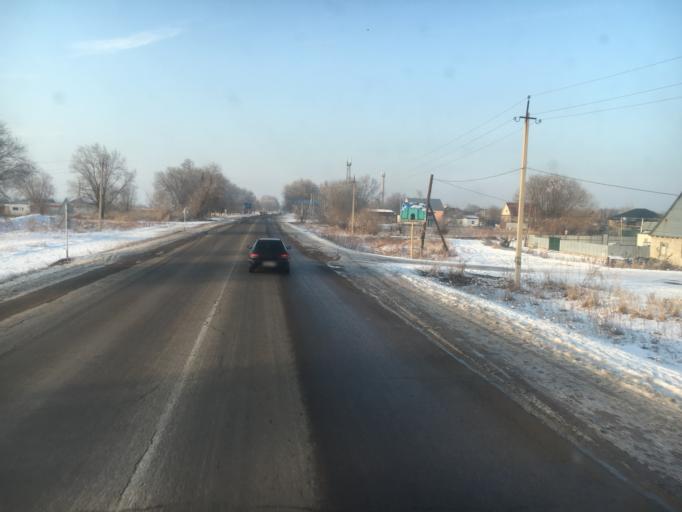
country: KZ
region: Almaty Oblysy
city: Burunday
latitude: 43.3334
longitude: 76.6612
